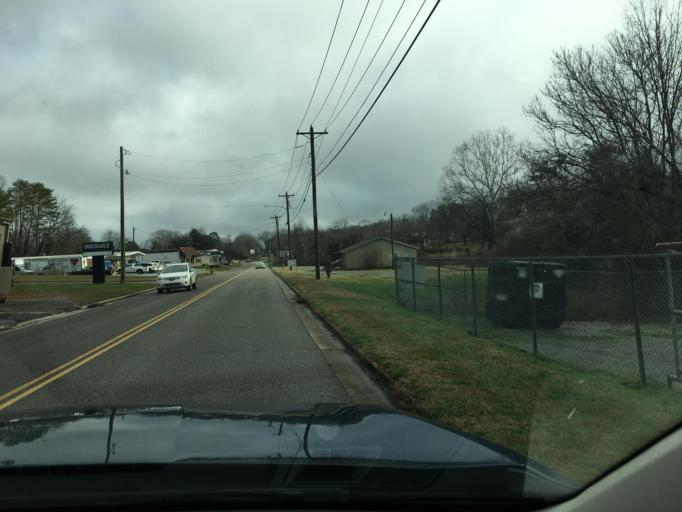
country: US
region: Tennessee
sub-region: McMinn County
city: Athens
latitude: 35.4395
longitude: -84.6225
